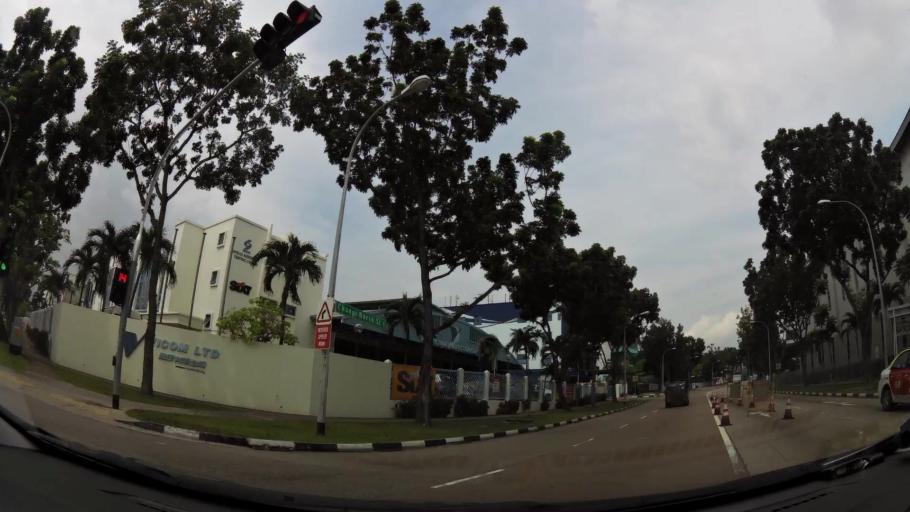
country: SG
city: Singapore
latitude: 1.3510
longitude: 103.9686
